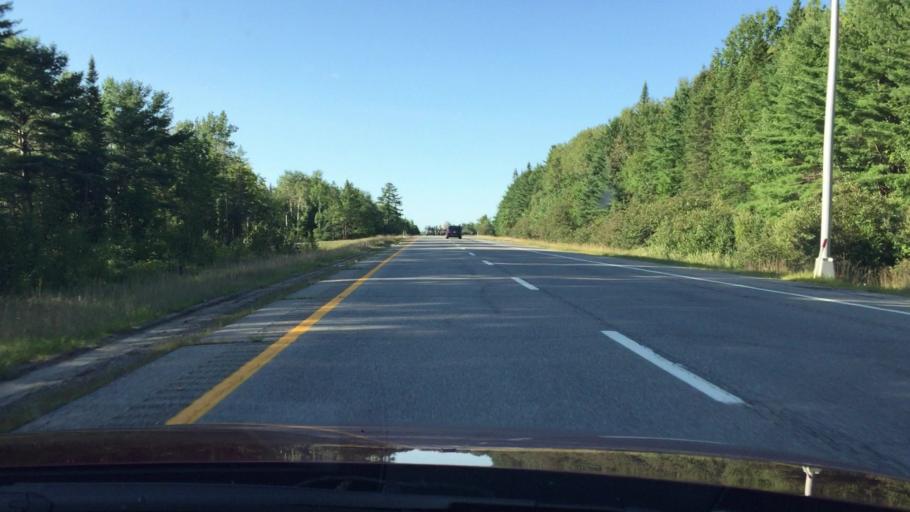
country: US
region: Maine
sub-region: Penobscot County
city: Lincoln
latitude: 45.3807
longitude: -68.6045
